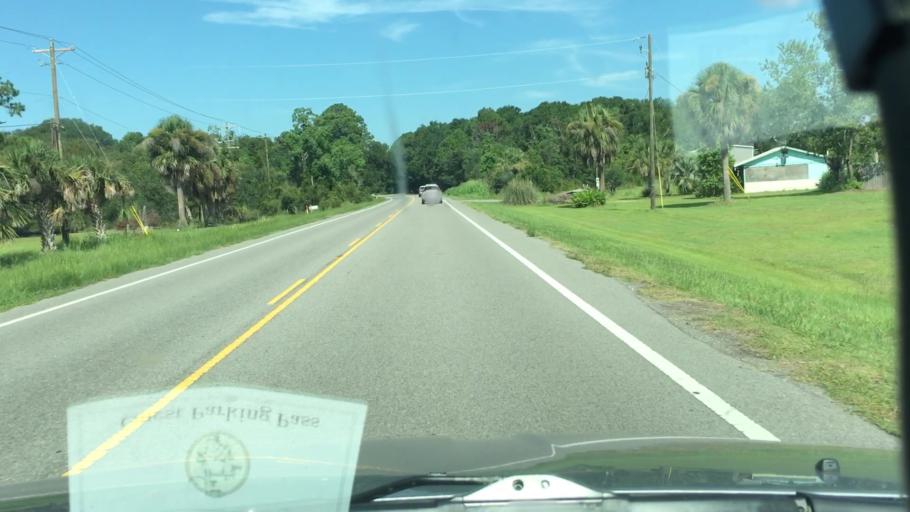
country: US
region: South Carolina
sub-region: Beaufort County
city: Beaufort
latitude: 32.4136
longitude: -80.4796
